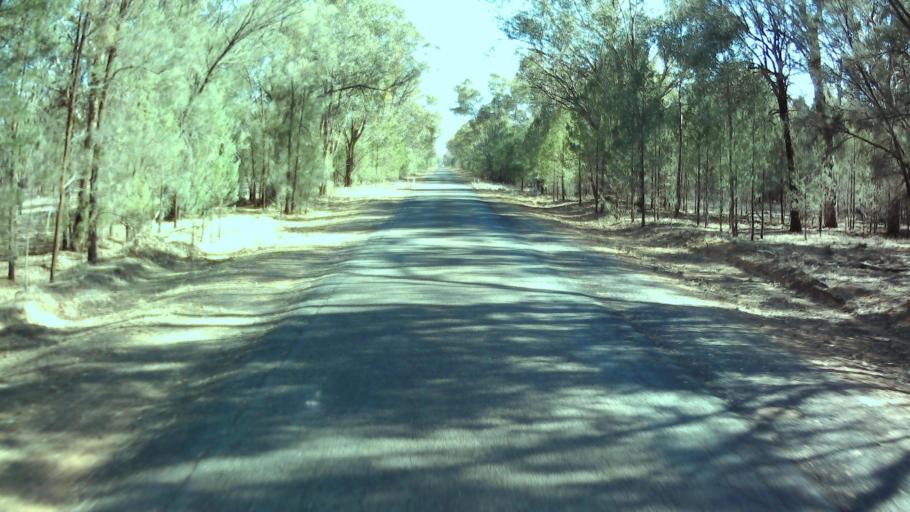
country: AU
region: New South Wales
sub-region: Weddin
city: Grenfell
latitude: -33.8133
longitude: 147.9536
